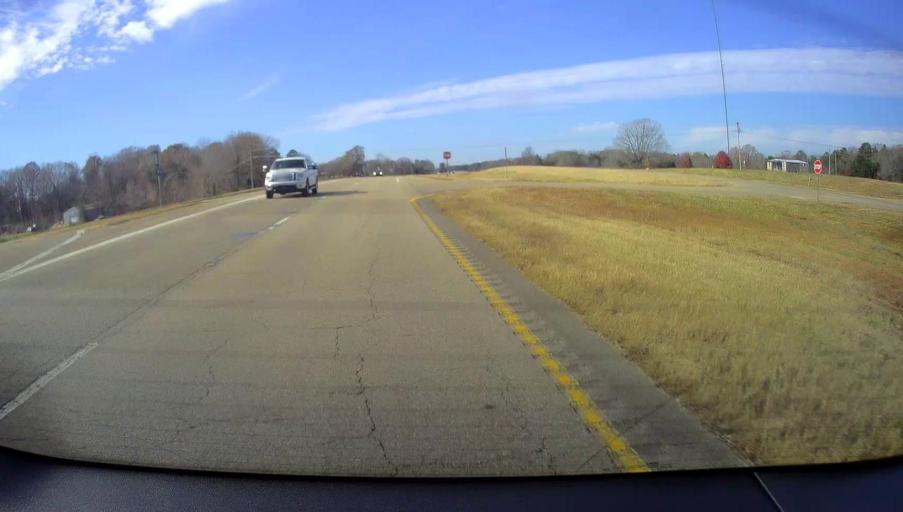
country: US
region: Mississippi
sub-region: Tippah County
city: Ripley
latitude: 34.9461
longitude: -88.8005
